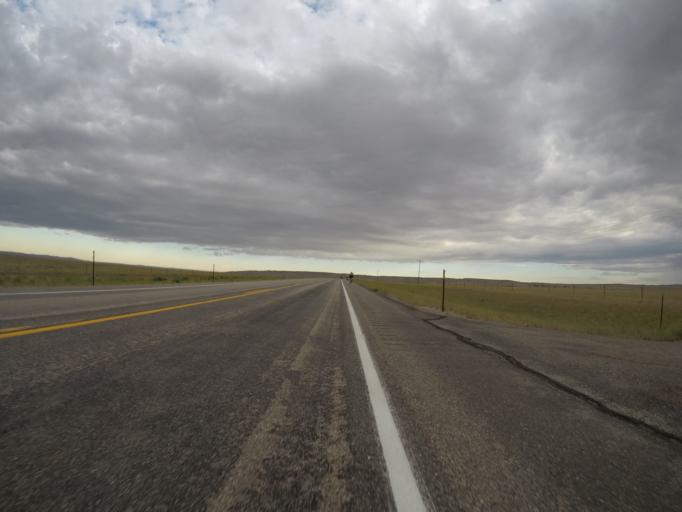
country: US
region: Wyoming
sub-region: Albany County
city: Laramie
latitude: 41.8508
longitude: -106.0419
